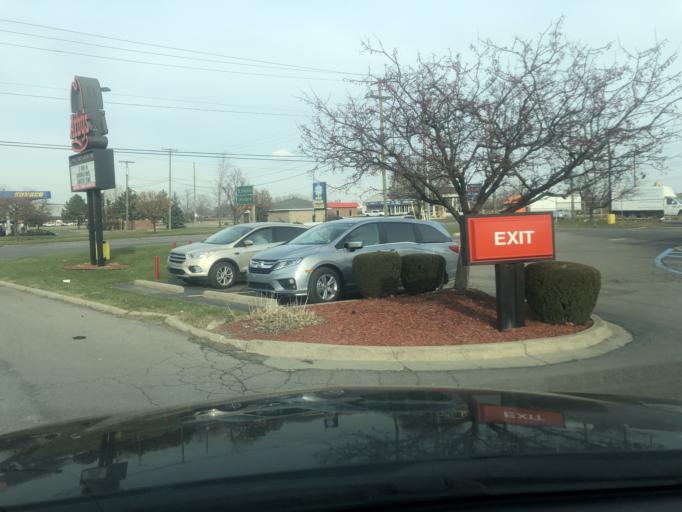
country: US
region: Michigan
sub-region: Wayne County
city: Southgate
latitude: 42.2128
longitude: -83.2254
